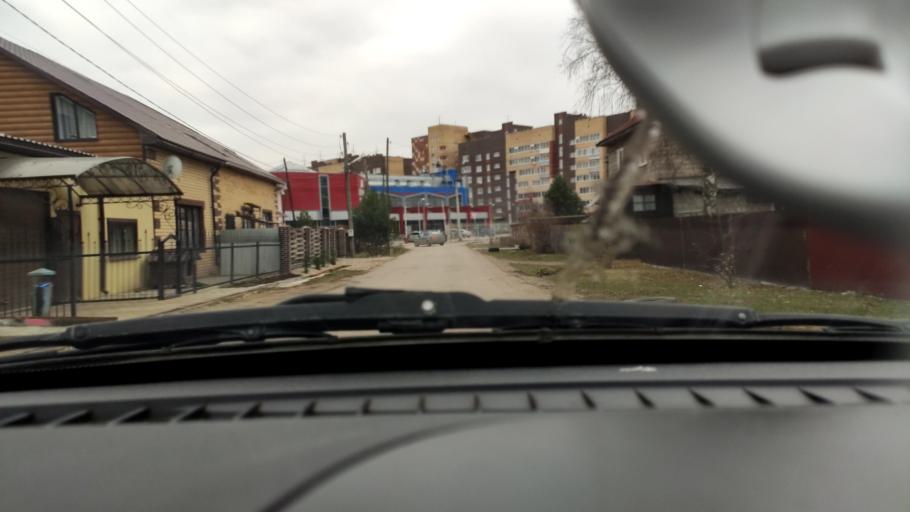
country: RU
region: Perm
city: Kondratovo
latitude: 57.9789
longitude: 56.0981
